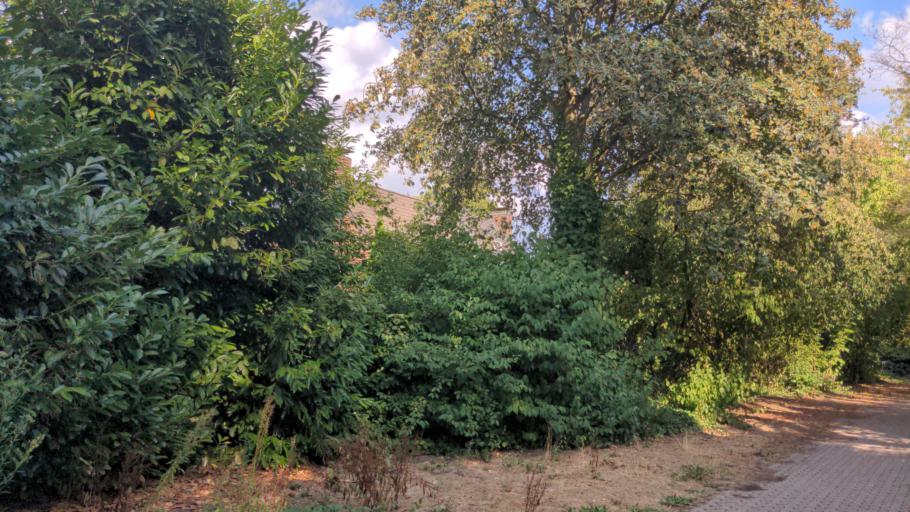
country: DE
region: North Rhine-Westphalia
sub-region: Regierungsbezirk Dusseldorf
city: Kaarst
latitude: 51.2123
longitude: 6.5804
